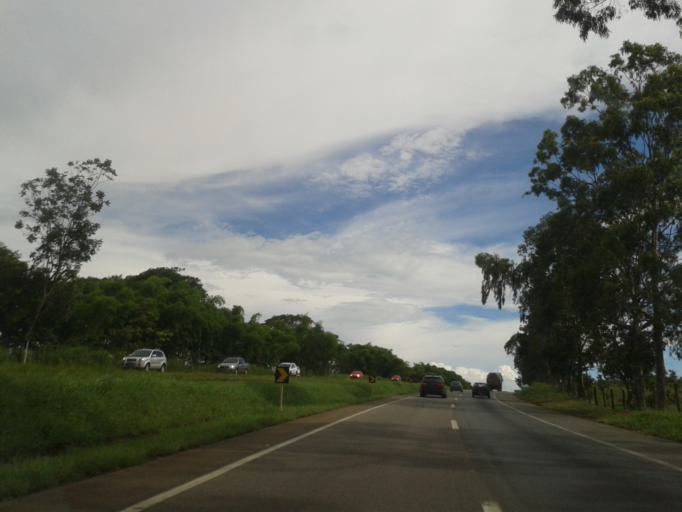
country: BR
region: Goias
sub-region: Hidrolandia
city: Hidrolandia
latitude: -16.9319
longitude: -49.2516
